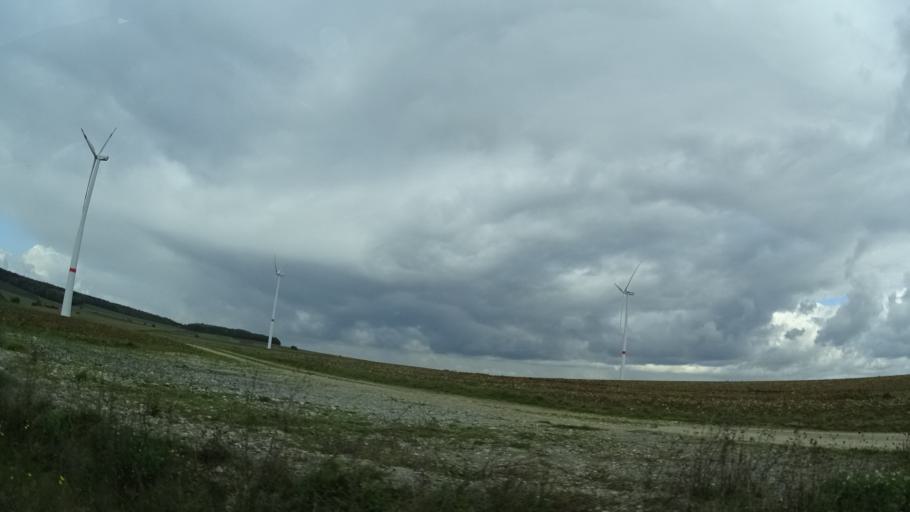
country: DE
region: Bavaria
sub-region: Regierungsbezirk Unterfranken
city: Geroldshausen
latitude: 49.6921
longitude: 9.8897
